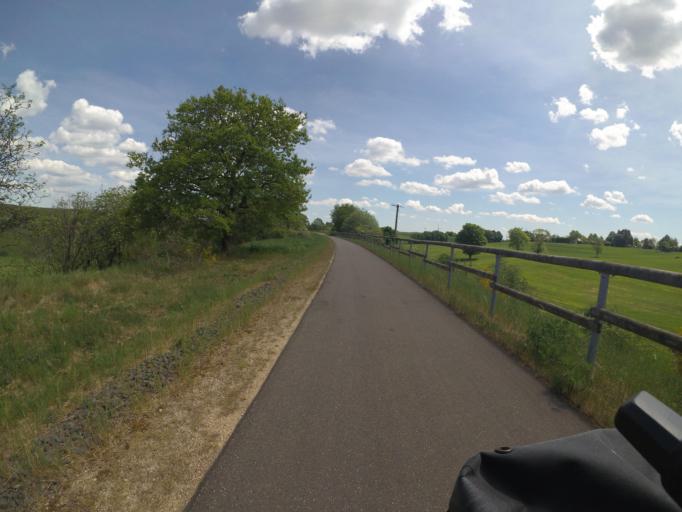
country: DE
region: Rheinland-Pfalz
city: Scheid
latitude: 50.3646
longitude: 6.3741
